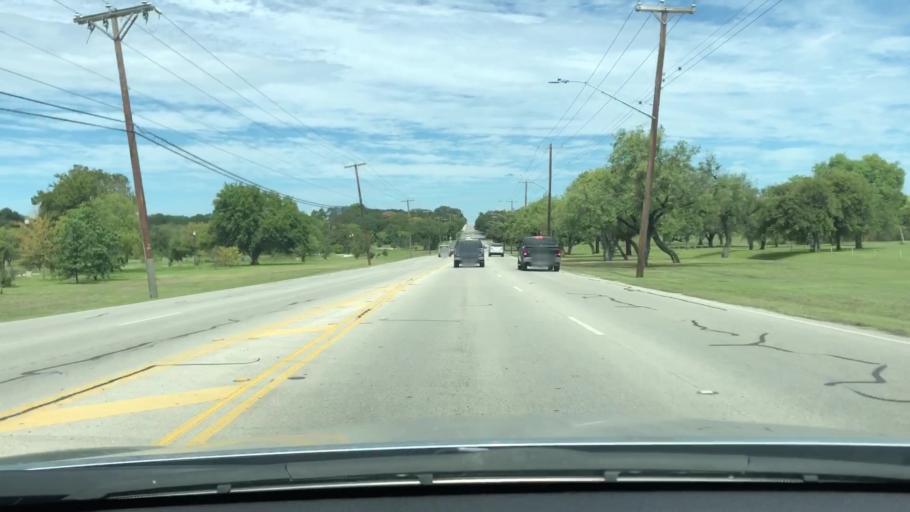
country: US
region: Texas
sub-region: Bexar County
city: Olmos Park
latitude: 29.4930
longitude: -98.4917
